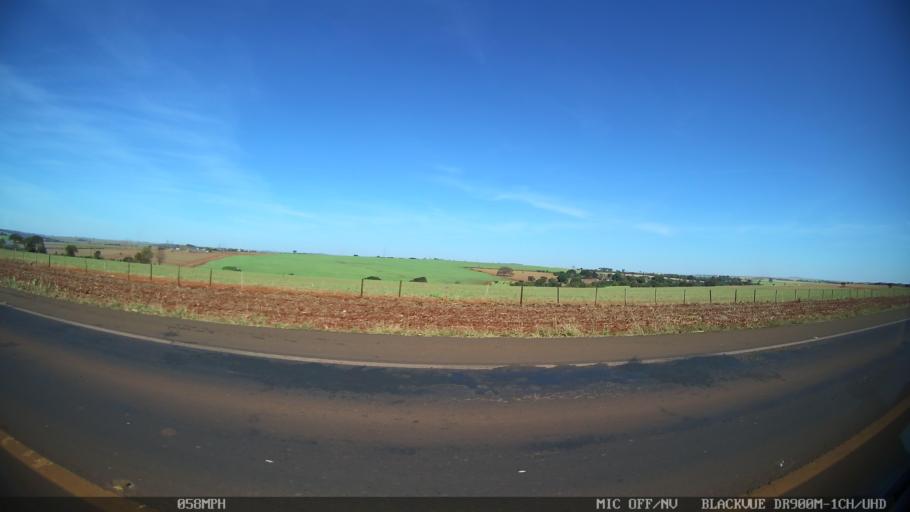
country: BR
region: Sao Paulo
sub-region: Sao Joaquim Da Barra
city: Sao Joaquim da Barra
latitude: -20.5226
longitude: -47.8543
